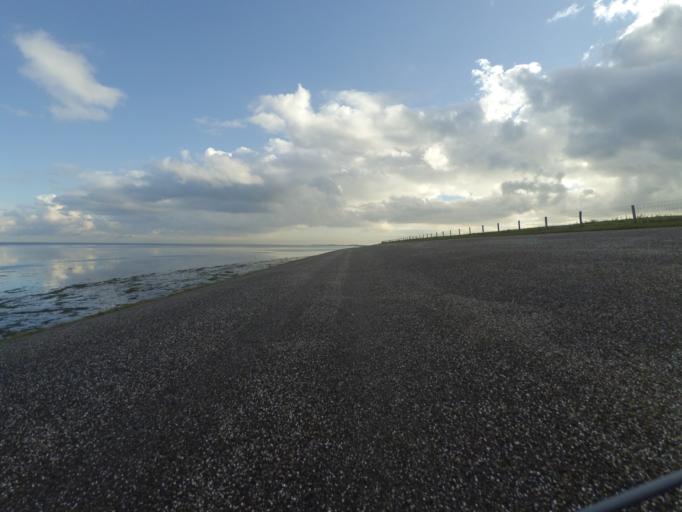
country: NL
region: North Holland
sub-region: Gemeente Hollands Kroon
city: Den Oever
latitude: 52.8983
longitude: 4.9173
